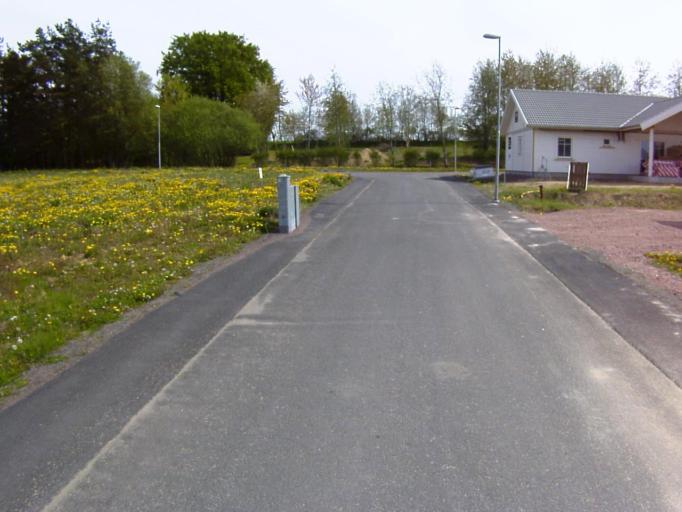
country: SE
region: Skane
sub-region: Kristianstads Kommun
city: Fjalkinge
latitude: 56.0774
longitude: 14.2178
